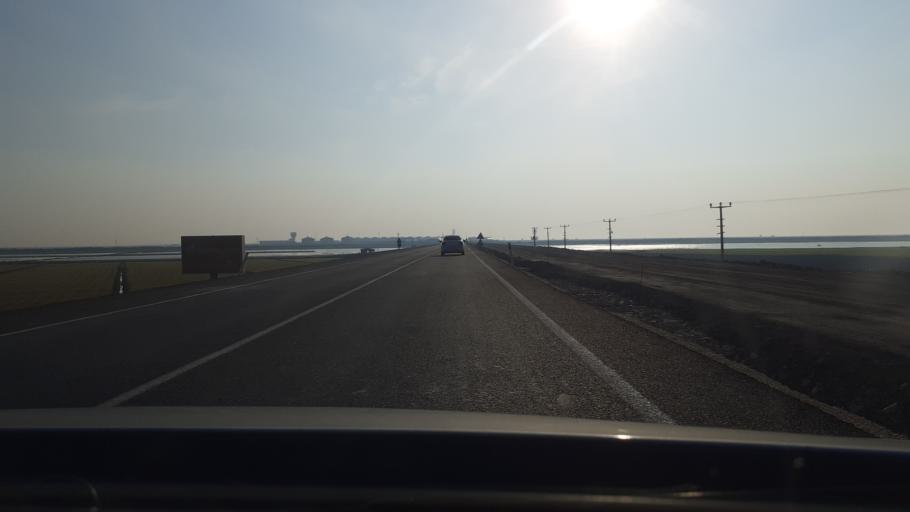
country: TR
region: Hatay
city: Serinyol
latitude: 36.3677
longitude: 36.2624
